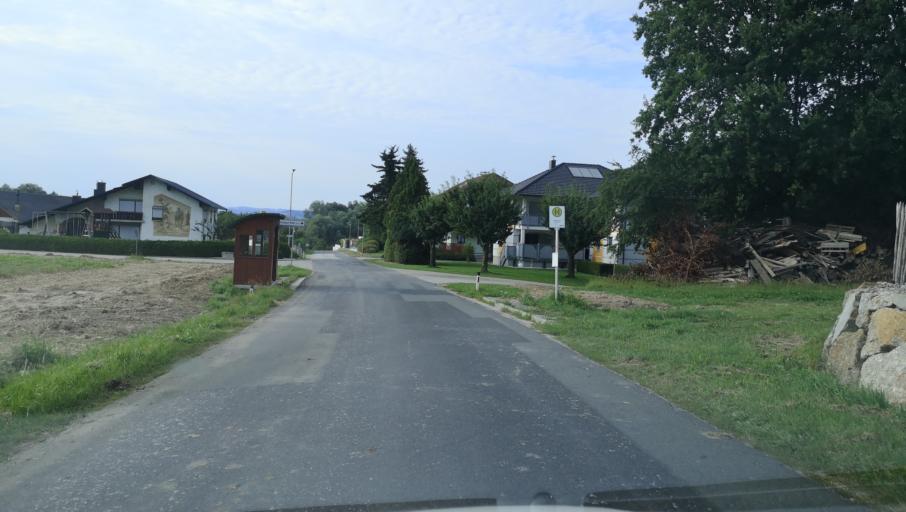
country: AT
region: Lower Austria
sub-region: Politischer Bezirk Amstetten
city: Zeillern
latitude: 48.1641
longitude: 14.8181
